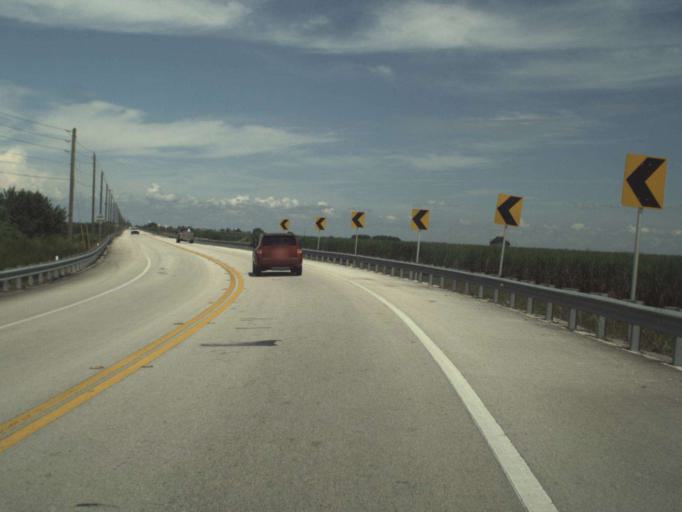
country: US
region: Florida
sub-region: Palm Beach County
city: Pahokee
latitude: 26.7710
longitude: -80.6533
